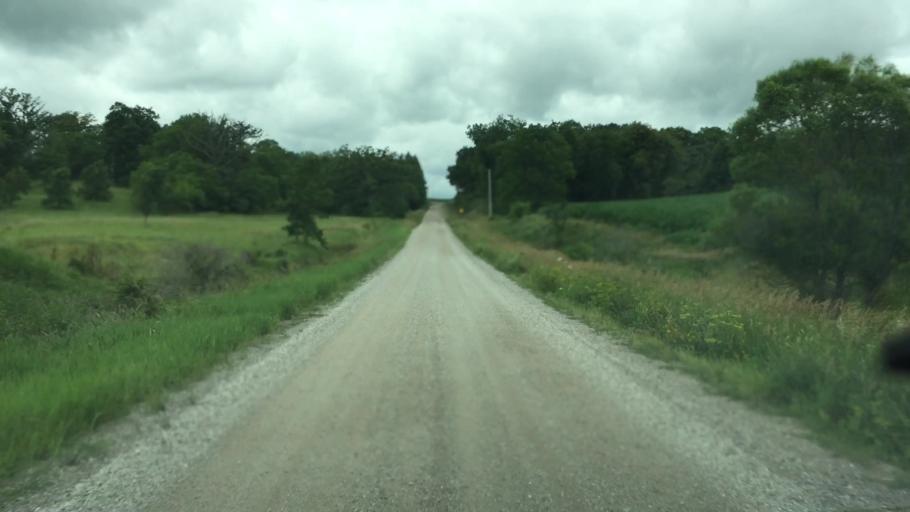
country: US
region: Iowa
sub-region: Jasper County
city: Monroe
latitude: 41.5952
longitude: -93.1106
